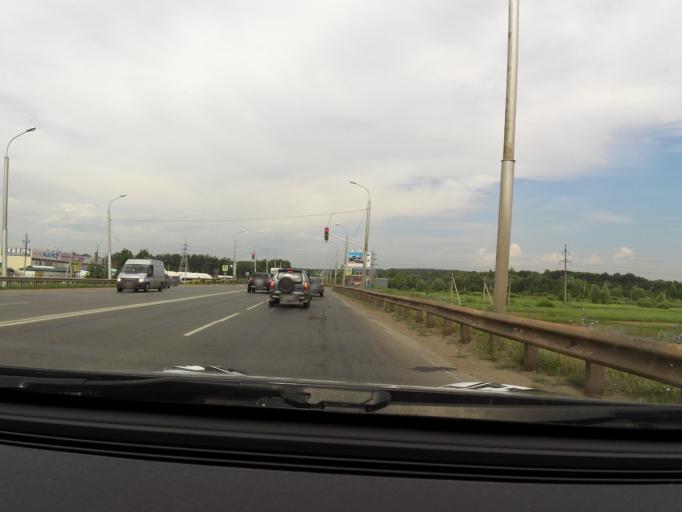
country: RU
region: Bashkortostan
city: Ufa
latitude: 54.8067
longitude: 56.1761
